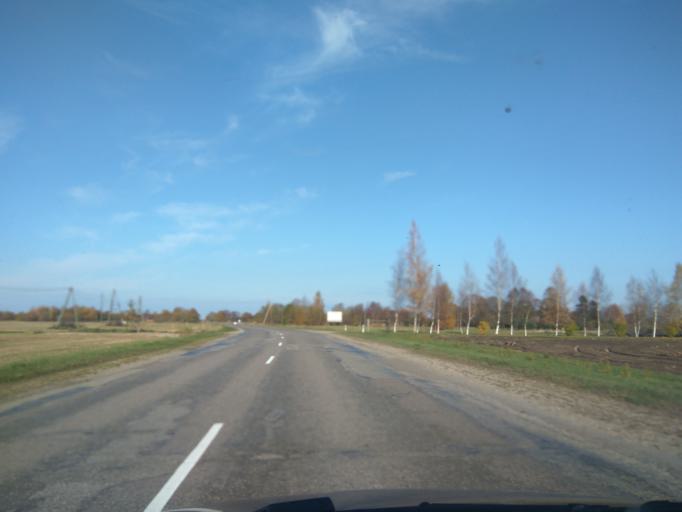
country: LV
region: Ventspils
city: Ventspils
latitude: 57.3252
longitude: 21.5640
